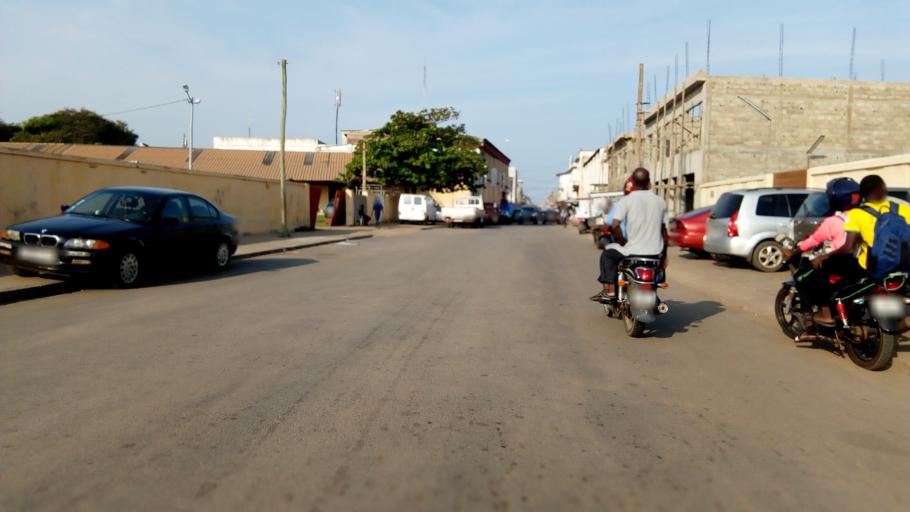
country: TG
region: Maritime
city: Lome
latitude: 6.1285
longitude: 1.2201
